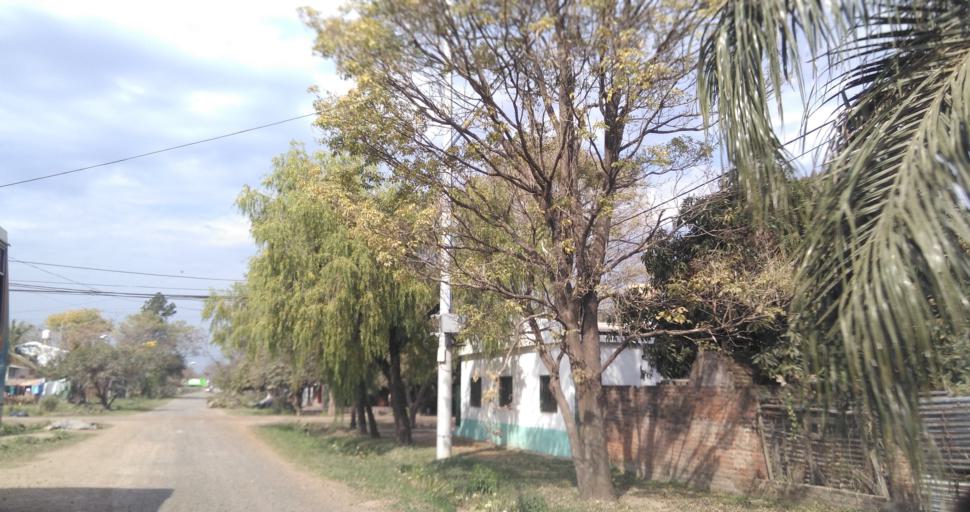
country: AR
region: Chaco
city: Fontana
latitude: -27.4532
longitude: -59.0359
